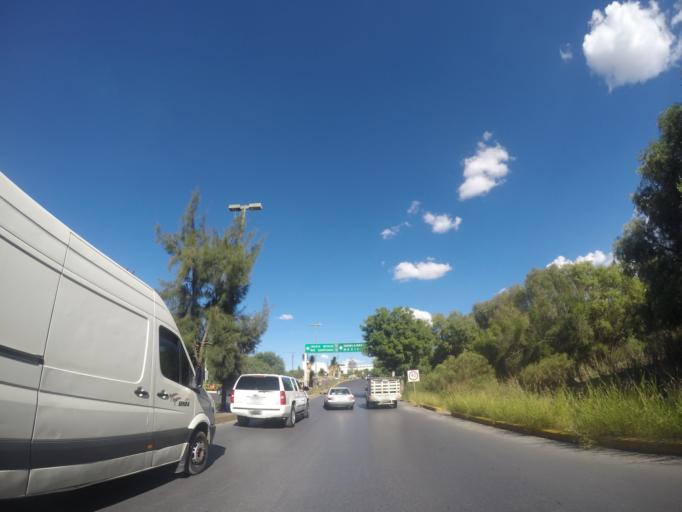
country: MX
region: San Luis Potosi
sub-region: Mexquitic de Carmona
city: Guadalupe Victoria
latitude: 22.1517
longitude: -101.0304
